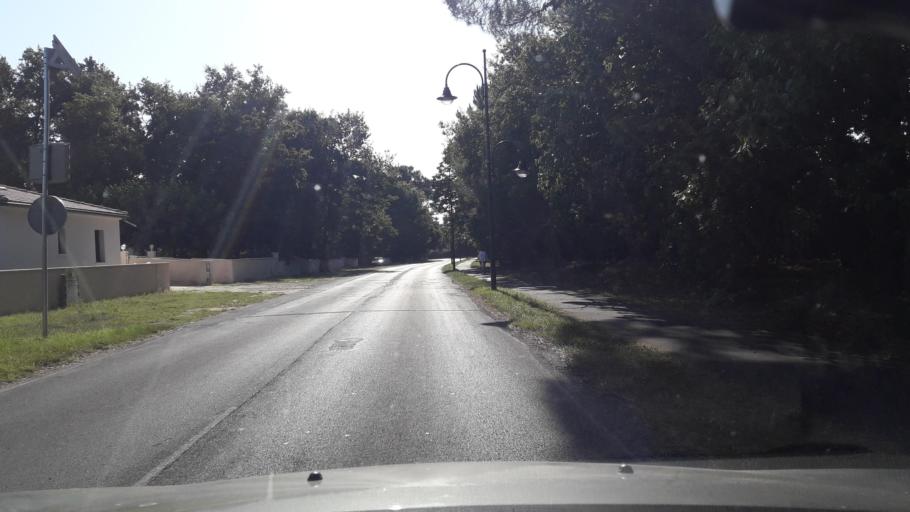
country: FR
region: Poitou-Charentes
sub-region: Departement de la Charente-Maritime
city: Les Mathes
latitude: 45.7138
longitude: -1.1417
